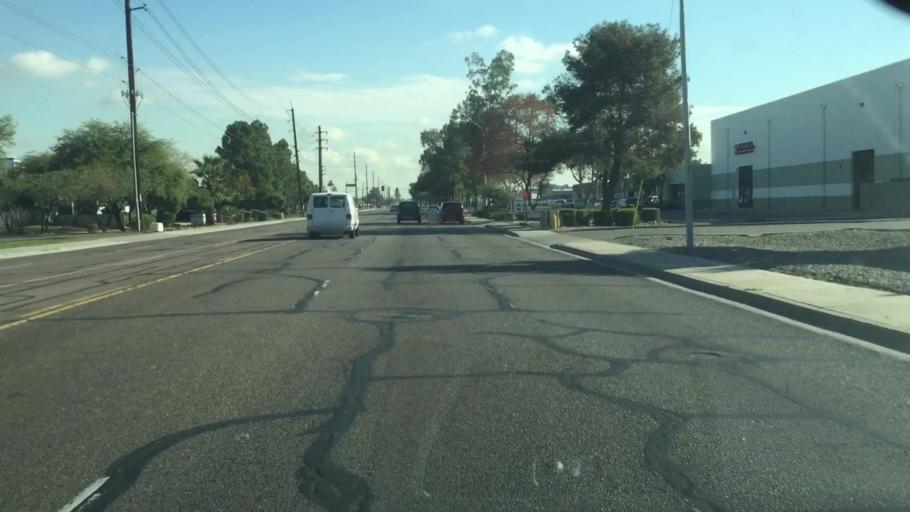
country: US
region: Arizona
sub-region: Maricopa County
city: Guadalupe
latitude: 33.4071
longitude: -112.0067
